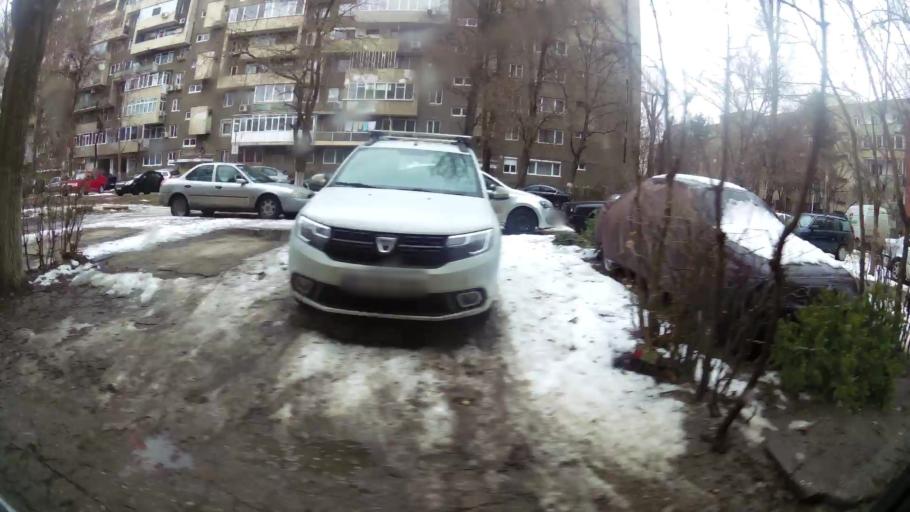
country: RO
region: Ilfov
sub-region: Comuna Chiajna
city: Rosu
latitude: 44.4236
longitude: 26.0301
